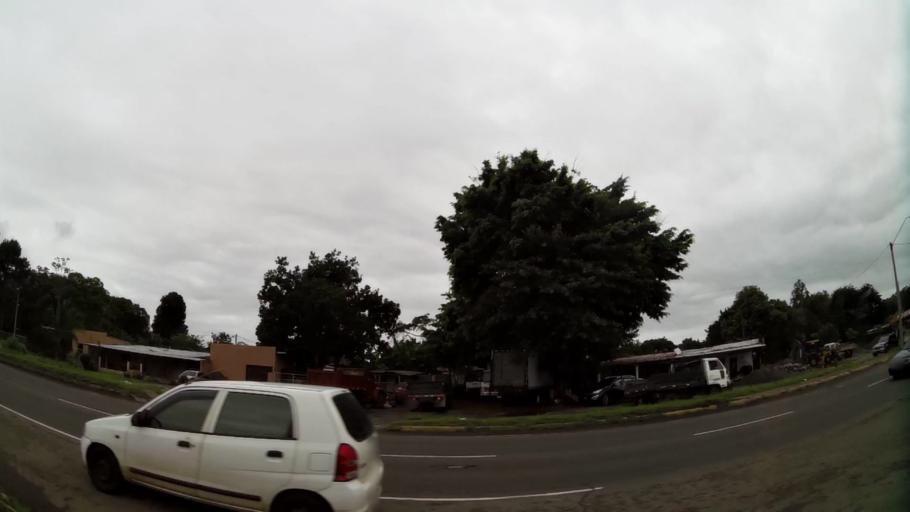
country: PA
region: Chiriqui
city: David
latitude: 8.4285
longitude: -82.4456
